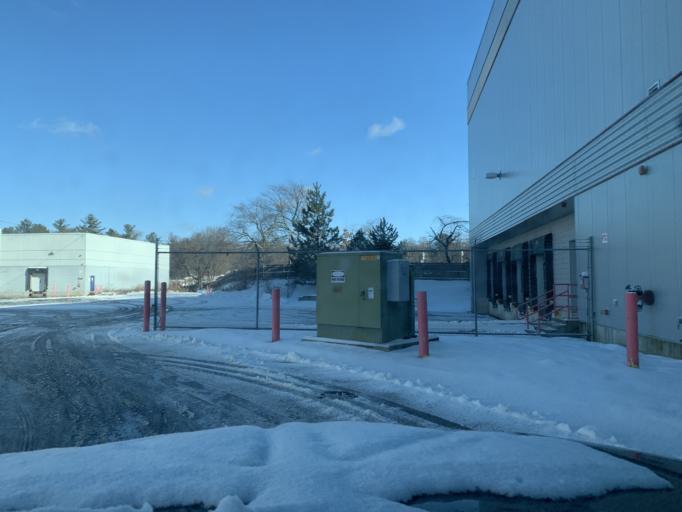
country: US
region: Massachusetts
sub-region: Essex County
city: Topsfield
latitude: 42.6001
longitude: -70.9615
